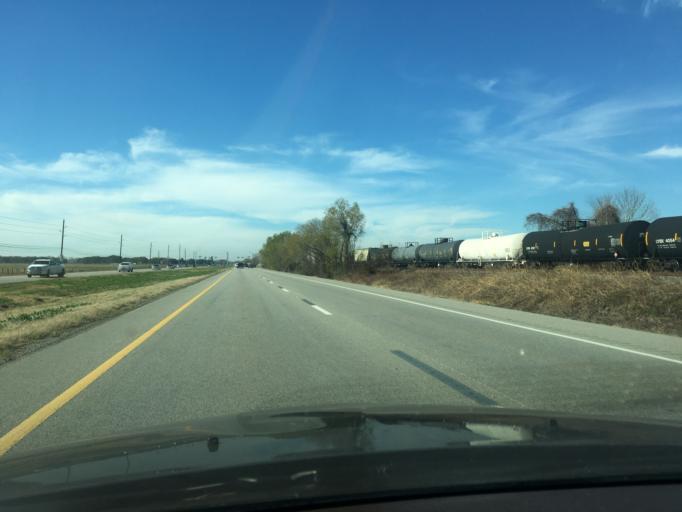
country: US
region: Texas
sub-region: Fort Bend County
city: New Territory
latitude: 29.5994
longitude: -95.7089
